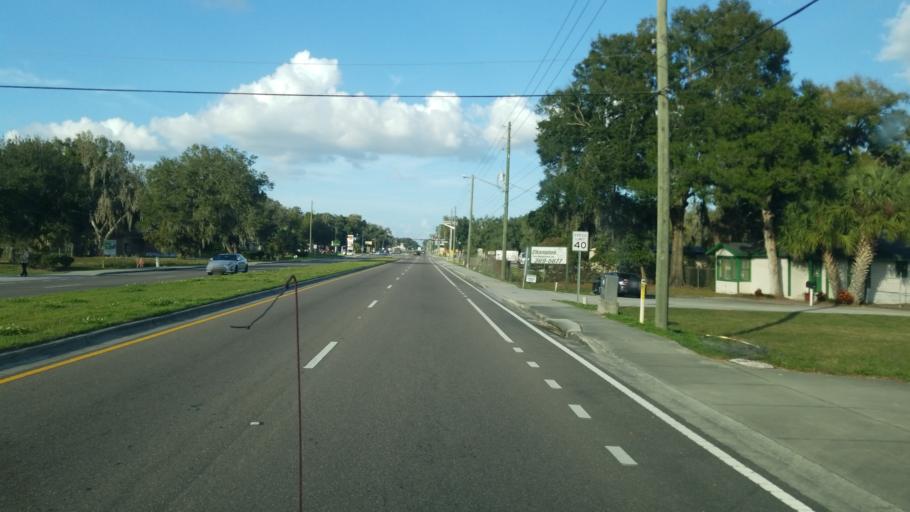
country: US
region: Florida
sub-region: Marion County
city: Ocala
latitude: 29.2130
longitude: -82.1266
